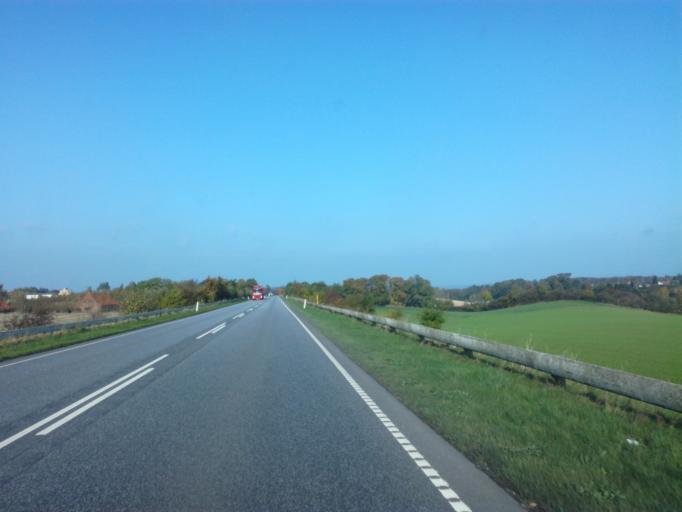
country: DK
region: South Denmark
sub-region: Fredericia Kommune
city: Fredericia
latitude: 55.6120
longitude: 9.7525
